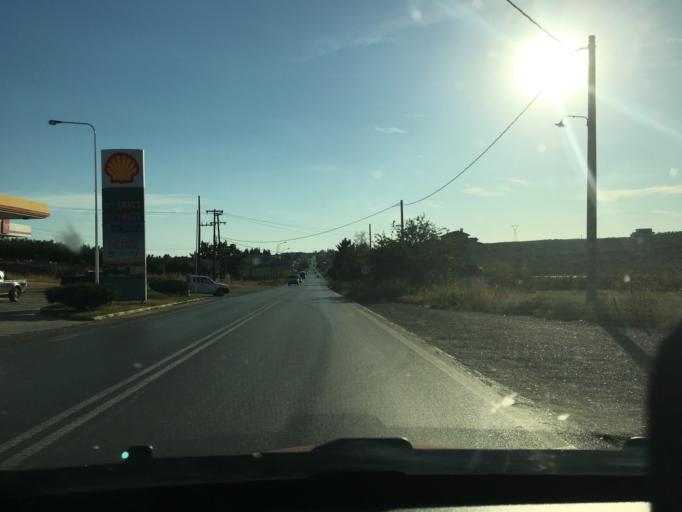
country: GR
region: Central Macedonia
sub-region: Nomos Chalkidikis
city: Olynthos
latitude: 40.2678
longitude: 23.3379
